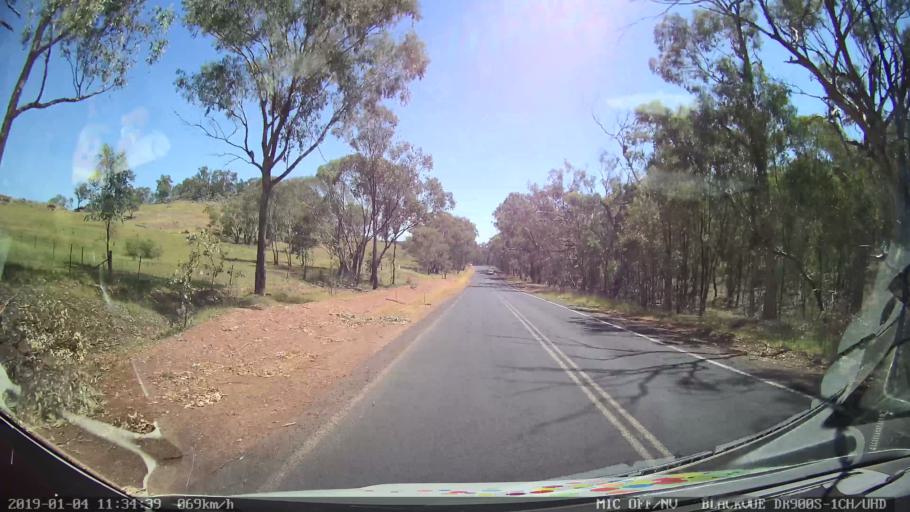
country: AU
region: New South Wales
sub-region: Cabonne
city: Molong
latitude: -33.0645
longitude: 148.8249
